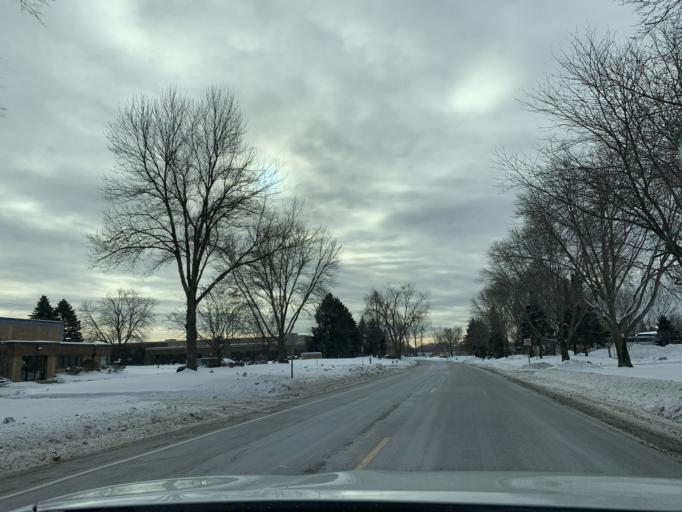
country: US
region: Minnesota
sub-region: Anoka County
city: Andover
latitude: 45.1794
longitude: -93.2981
